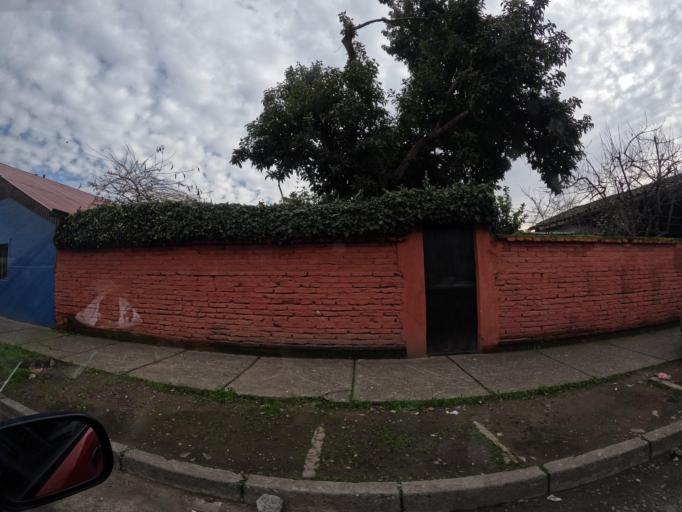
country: CL
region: Maule
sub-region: Provincia de Linares
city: Linares
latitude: -35.8525
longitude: -71.5854
